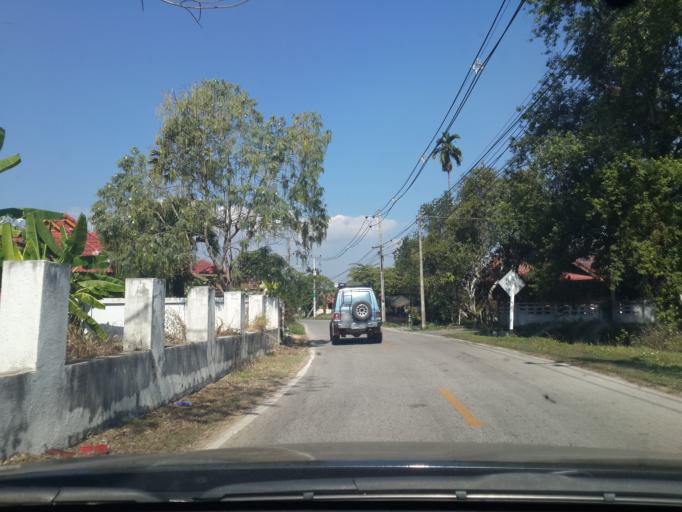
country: TH
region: Chiang Mai
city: San Sai
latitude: 18.8683
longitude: 99.0949
